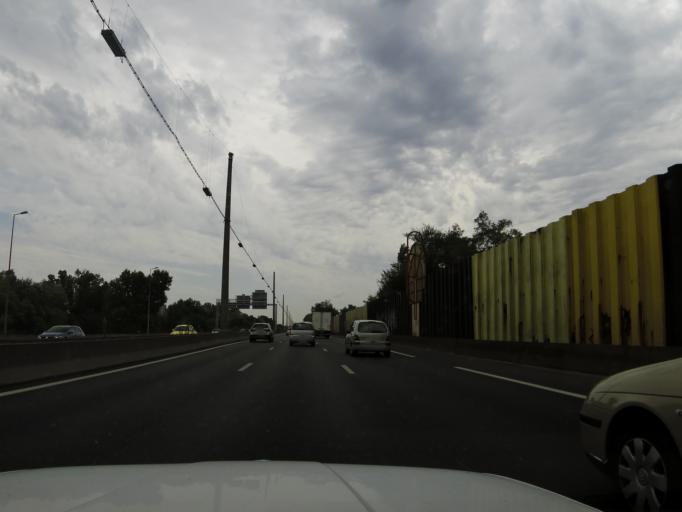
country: FR
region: Rhone-Alpes
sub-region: Departement du Rhone
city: Villeurbanne
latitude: 45.7791
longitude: 4.8952
